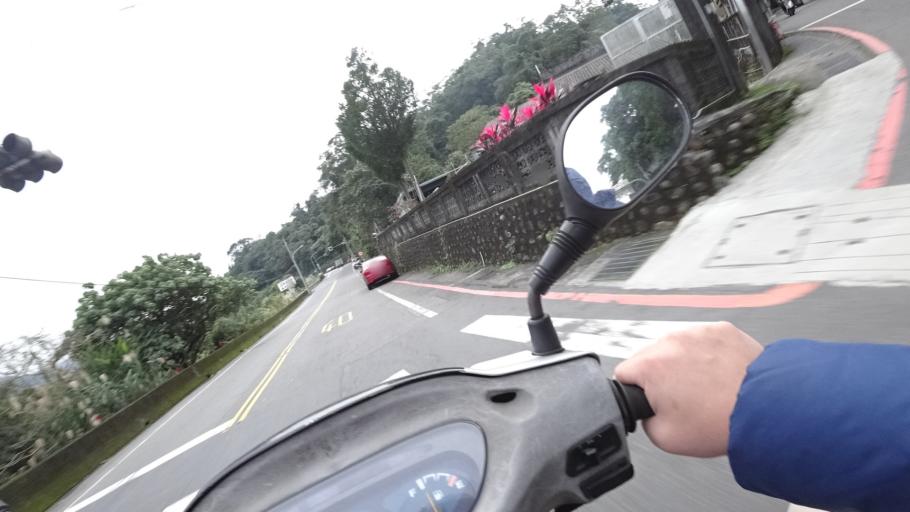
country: TW
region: Taipei
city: Taipei
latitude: 25.0075
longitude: 121.6271
